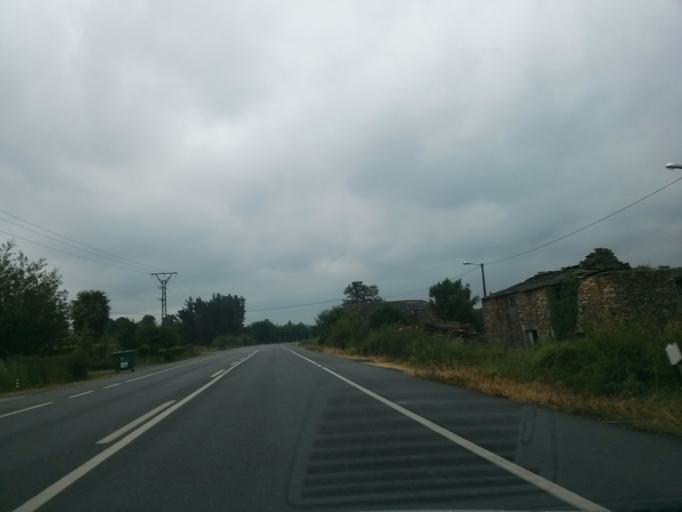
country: ES
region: Galicia
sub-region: Provincia de Lugo
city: Begonte
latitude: 43.1637
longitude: -7.7056
